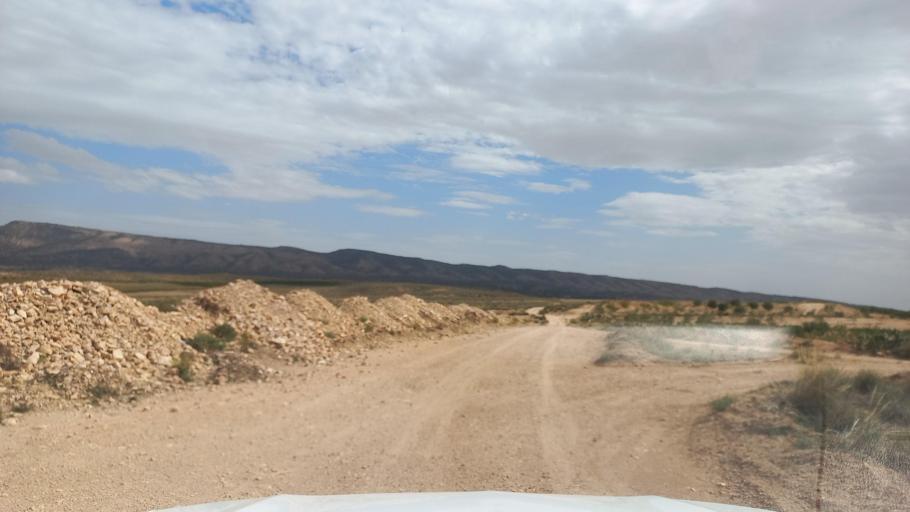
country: TN
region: Al Qasrayn
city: Sbiba
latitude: 35.3591
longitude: 9.1140
